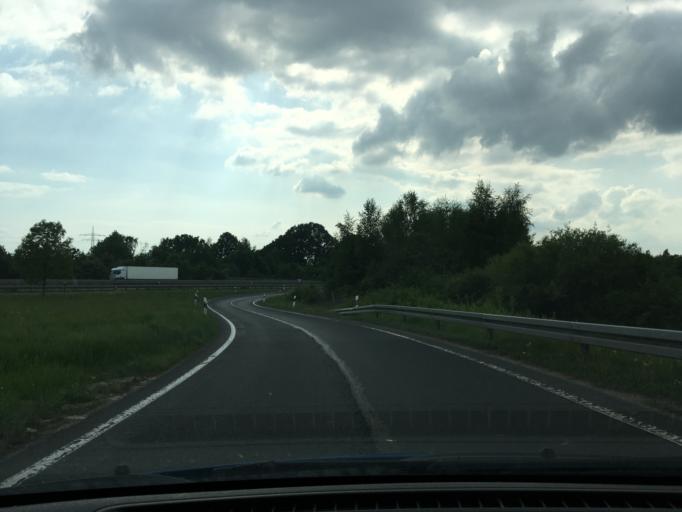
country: DE
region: Lower Saxony
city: Lehrte
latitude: 52.3912
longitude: 9.9617
